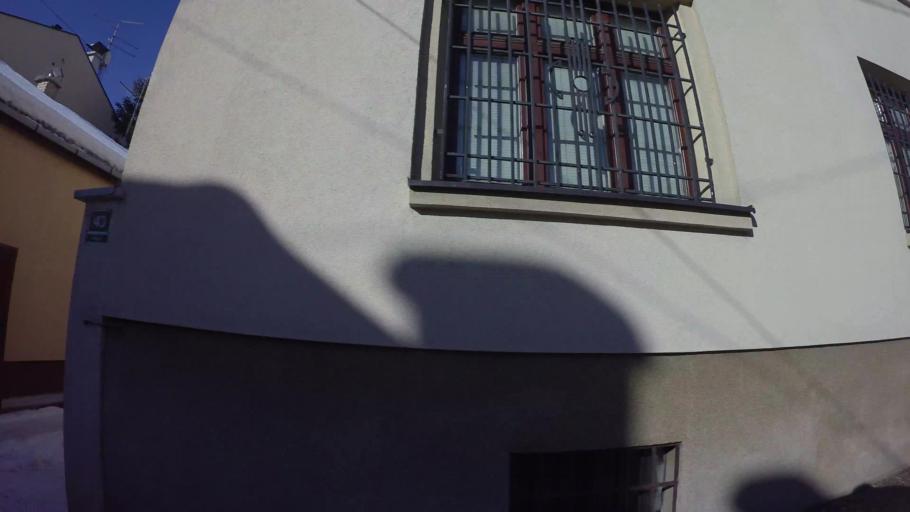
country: BA
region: Federation of Bosnia and Herzegovina
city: Kobilja Glava
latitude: 43.8642
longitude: 18.4189
